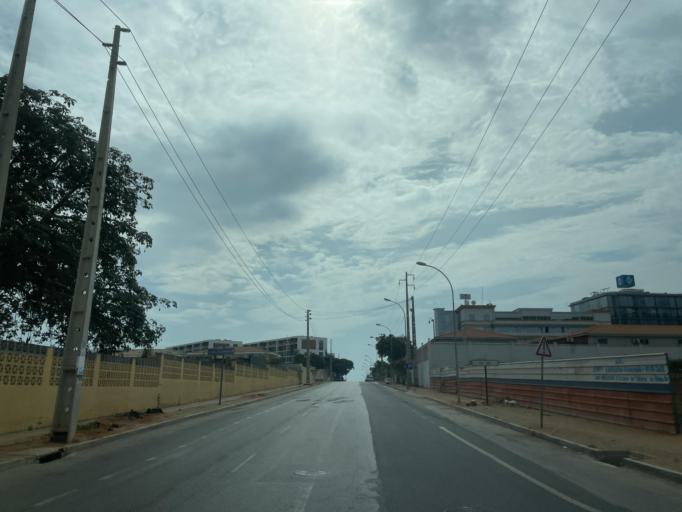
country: AO
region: Luanda
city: Luanda
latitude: -8.9214
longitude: 13.1754
